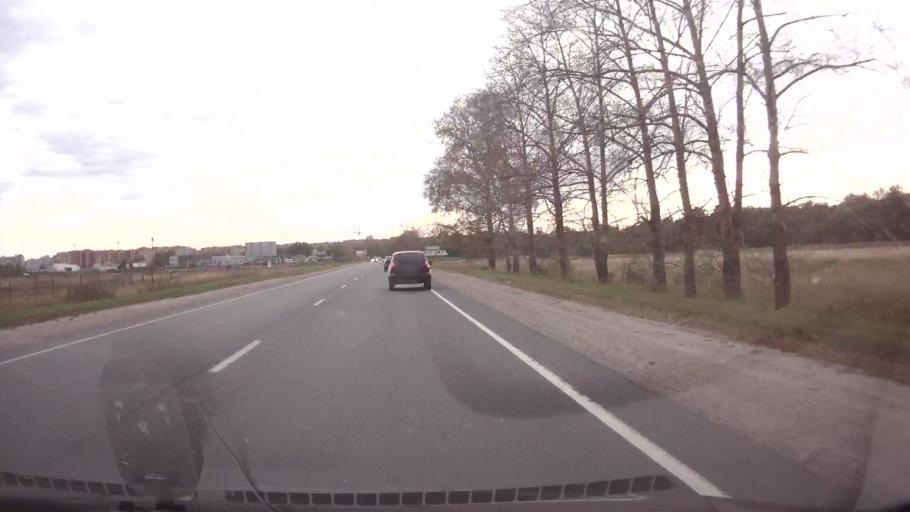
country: RU
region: Mariy-El
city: Yoshkar-Ola
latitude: 56.6487
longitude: 47.9425
